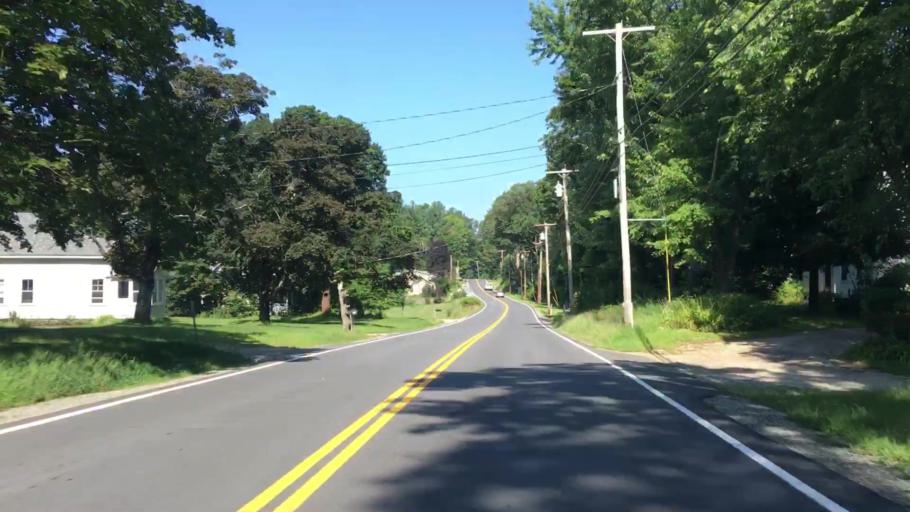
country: US
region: New Hampshire
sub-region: Rockingham County
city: East Kingston
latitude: 42.9261
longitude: -71.0181
